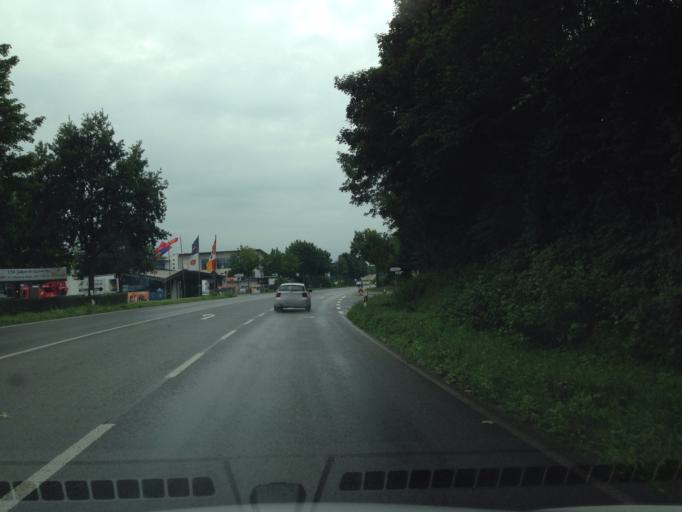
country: DE
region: North Rhine-Westphalia
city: Erkelenz
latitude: 51.0744
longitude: 6.3306
